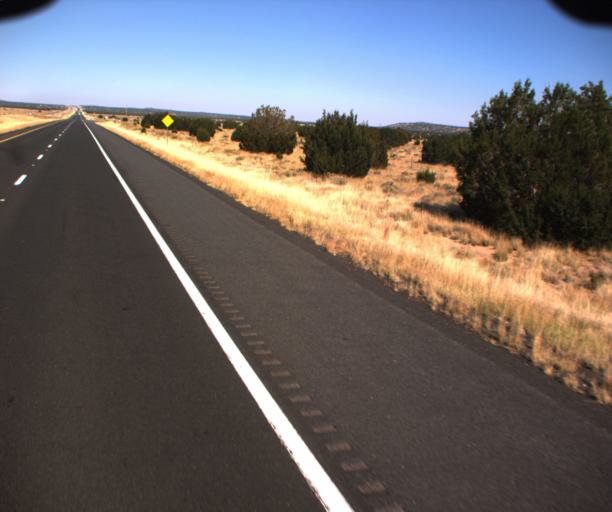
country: US
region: Arizona
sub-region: Coconino County
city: Flagstaff
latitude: 35.4382
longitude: -111.5661
